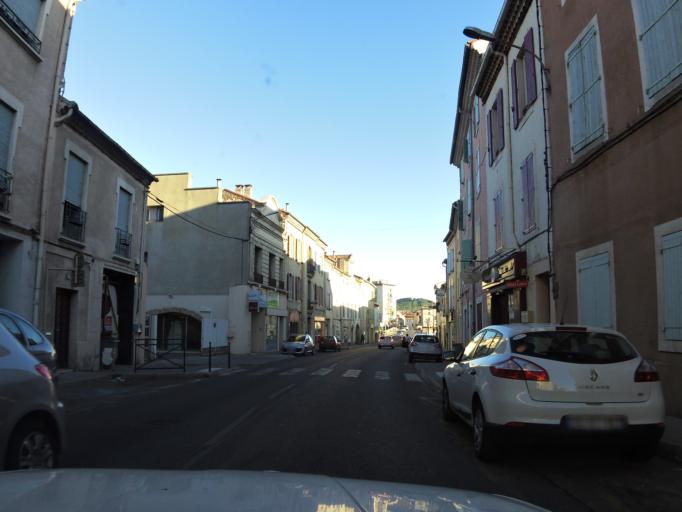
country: FR
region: Languedoc-Roussillon
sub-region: Departement du Gard
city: Ales
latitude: 44.1190
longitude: 4.0795
